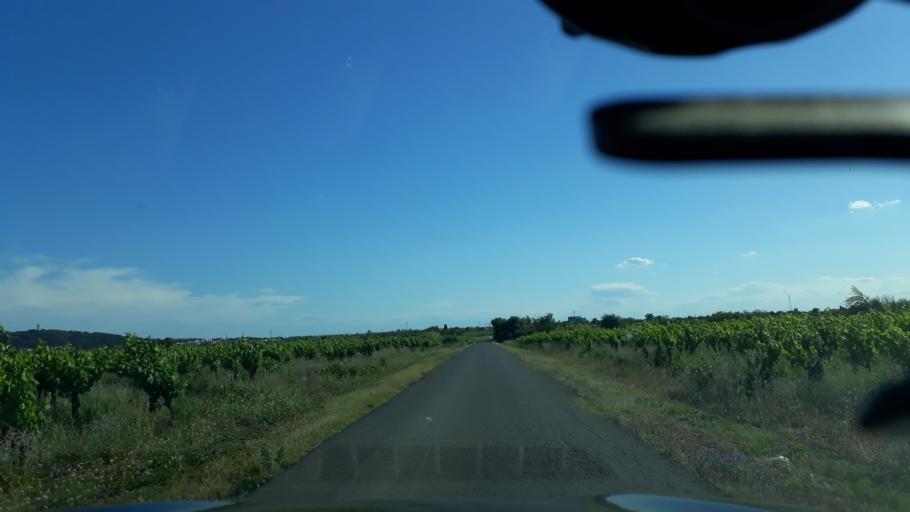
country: FR
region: Languedoc-Roussillon
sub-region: Departement de l'Herault
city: Agde
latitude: 43.3309
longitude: 3.5012
